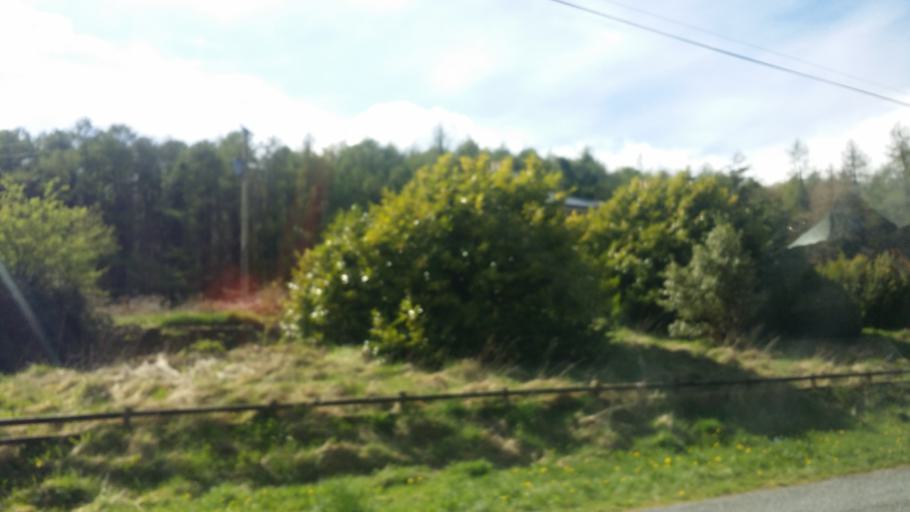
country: GB
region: Northern Ireland
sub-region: Fermanagh District
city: Enniskillen
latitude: 54.4112
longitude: -7.7247
